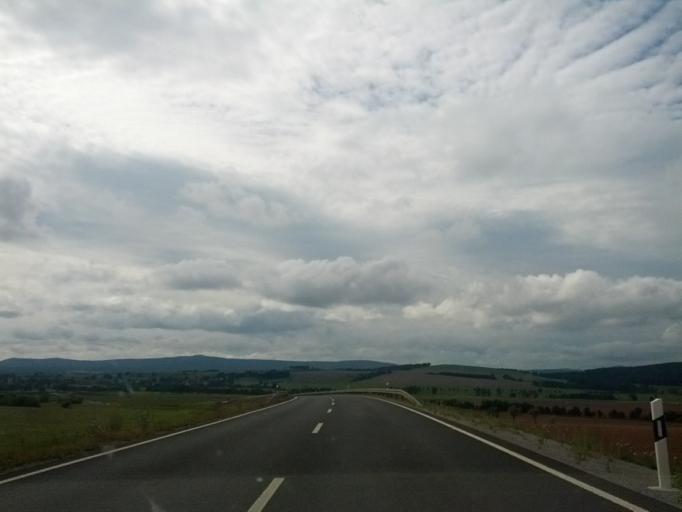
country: DE
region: Thuringia
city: Barchfeld
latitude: 50.8480
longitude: 10.2861
